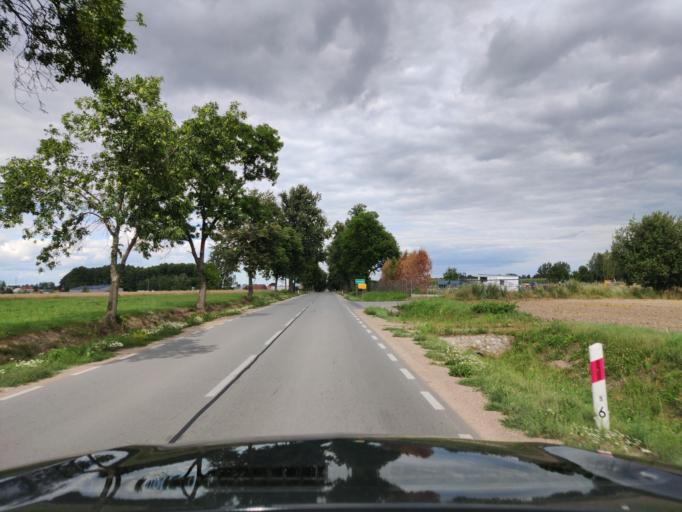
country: PL
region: Masovian Voivodeship
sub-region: Powiat sokolowski
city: Ceranow
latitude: 52.6223
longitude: 22.2135
